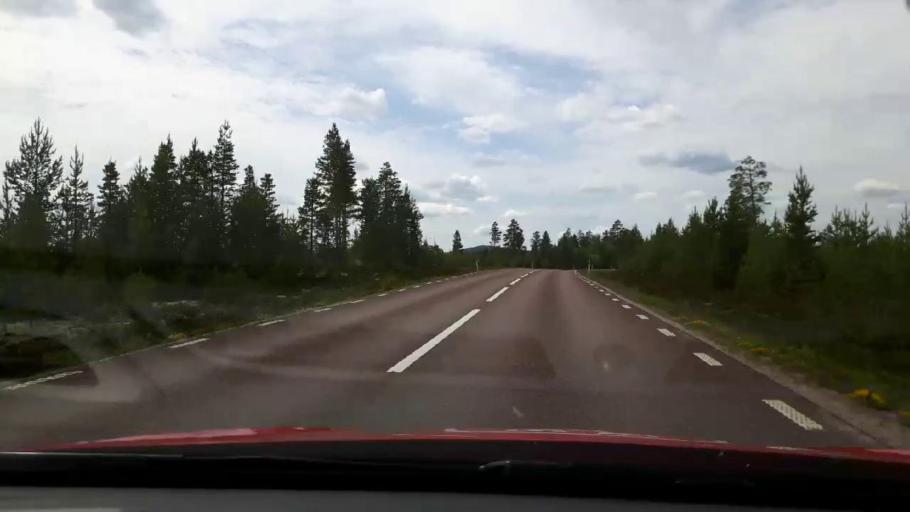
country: SE
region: Jaemtland
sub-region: Harjedalens Kommun
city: Sveg
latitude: 62.0406
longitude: 14.4621
